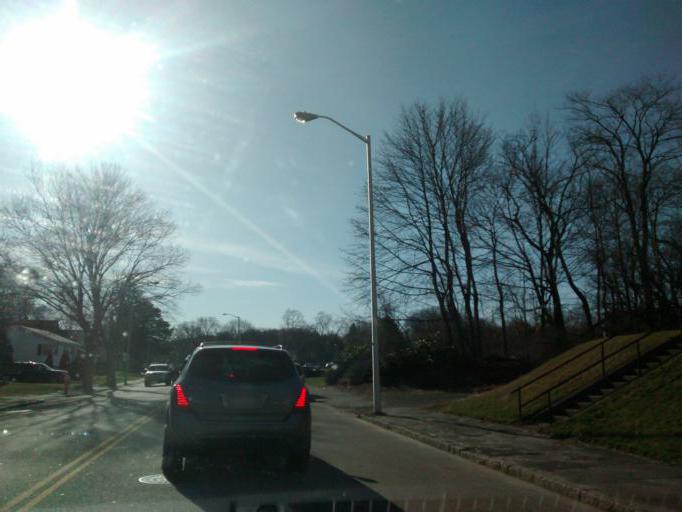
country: US
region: Massachusetts
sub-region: Worcester County
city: Worcester
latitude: 42.2902
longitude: -71.8135
